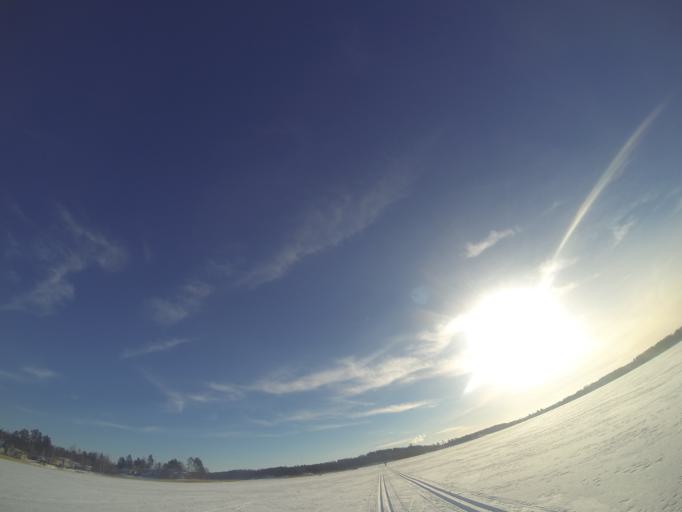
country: FI
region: Southern Savonia
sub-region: Savonlinna
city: Savonlinna
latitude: 61.8856
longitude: 28.9046
